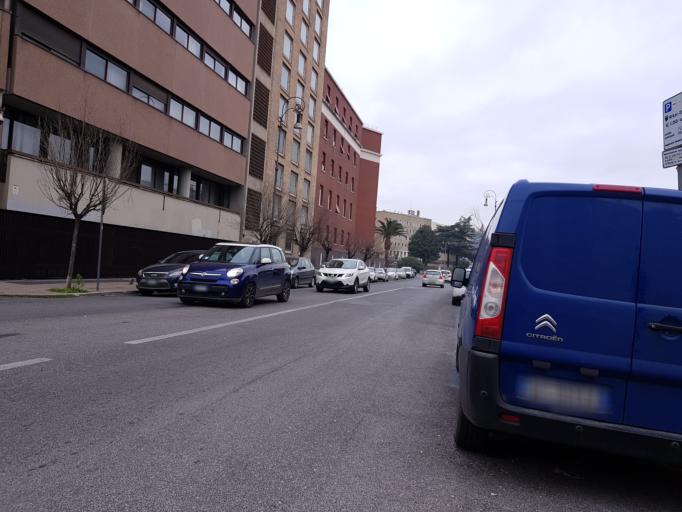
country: IT
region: Latium
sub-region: Citta metropolitana di Roma Capitale
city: Rome
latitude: 41.9004
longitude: 12.5139
